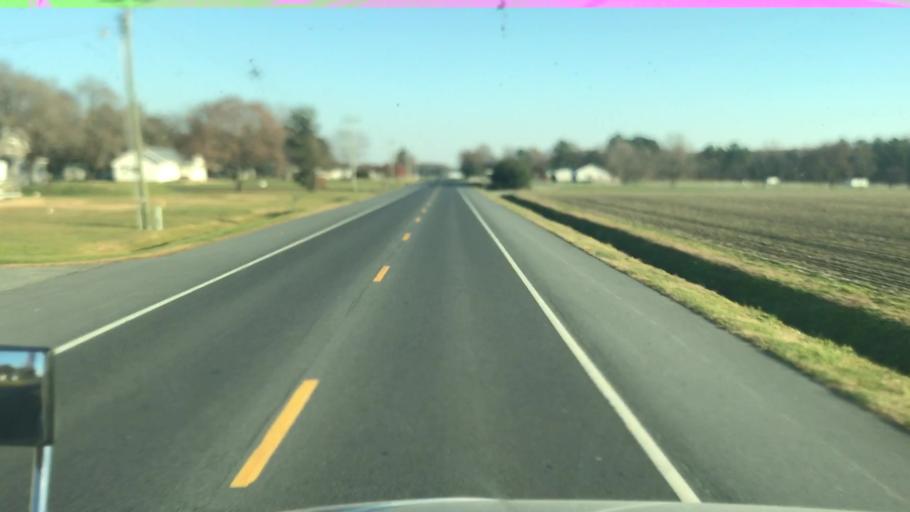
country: US
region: Delaware
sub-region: Sussex County
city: Bridgeville
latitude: 38.7839
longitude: -75.6751
